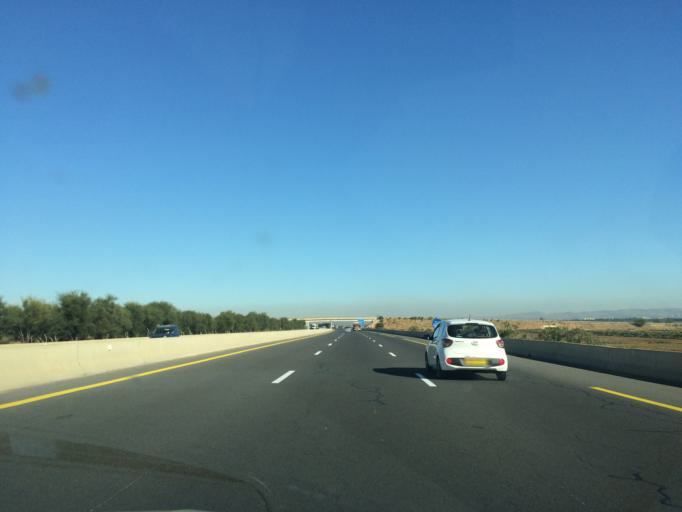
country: DZ
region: Relizane
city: Relizane
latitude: 35.8072
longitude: 0.6215
